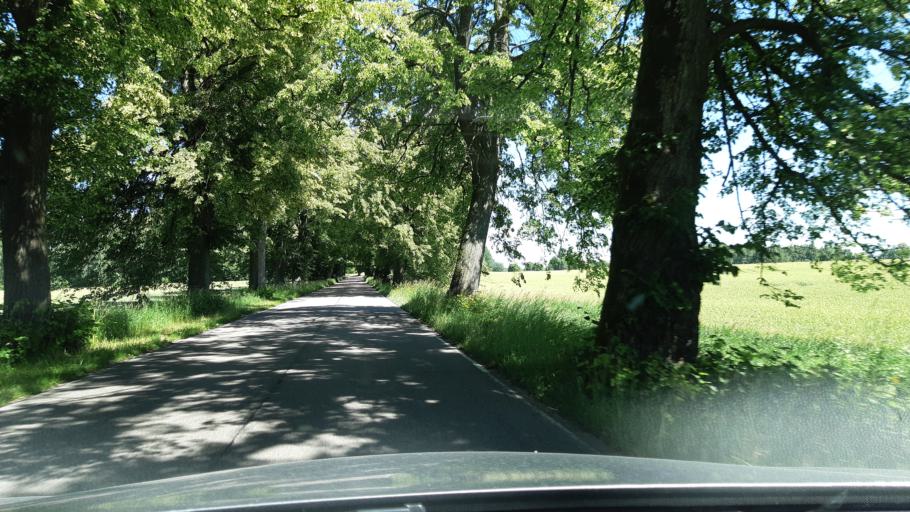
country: PL
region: Warmian-Masurian Voivodeship
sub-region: Powiat gizycki
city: Ryn
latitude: 53.9046
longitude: 21.6683
